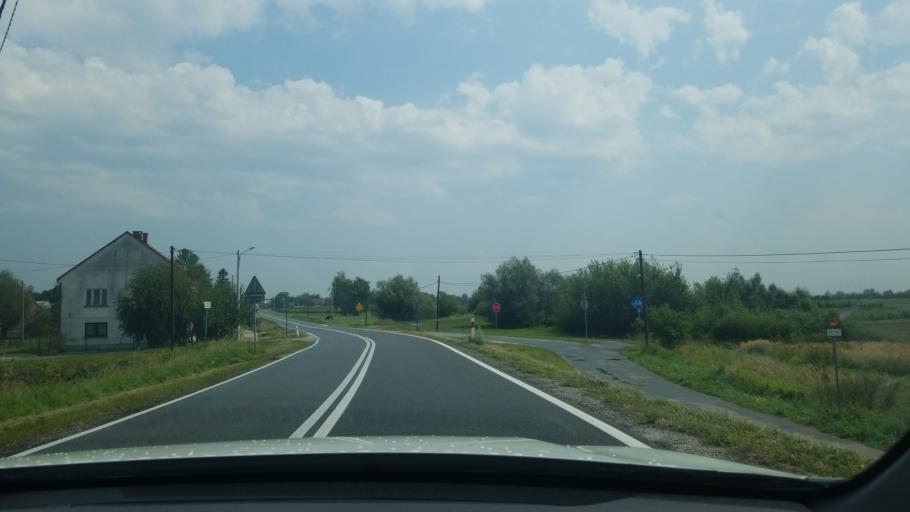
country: PL
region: Lesser Poland Voivodeship
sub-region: Powiat bochenski
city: Dziewin
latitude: 50.1225
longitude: 20.4769
